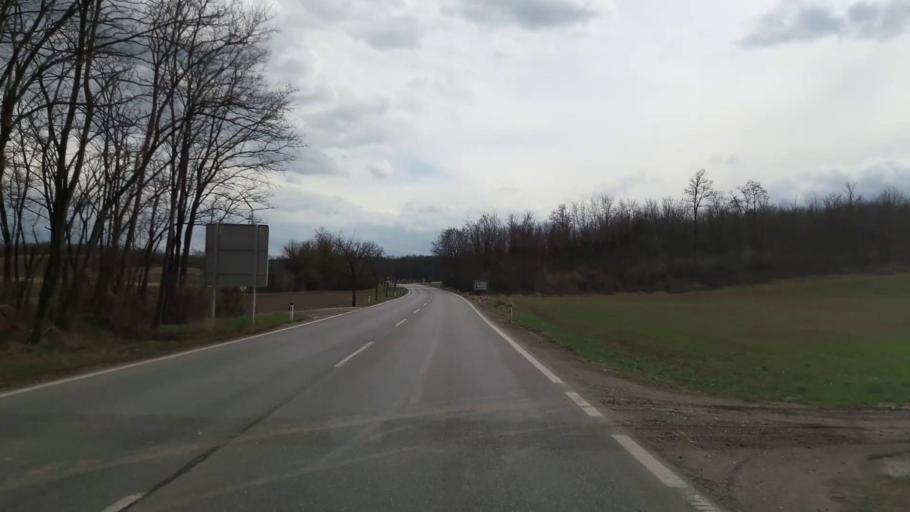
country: AT
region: Lower Austria
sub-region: Politischer Bezirk Mistelbach
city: Mistelbach
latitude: 48.5448
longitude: 16.5892
